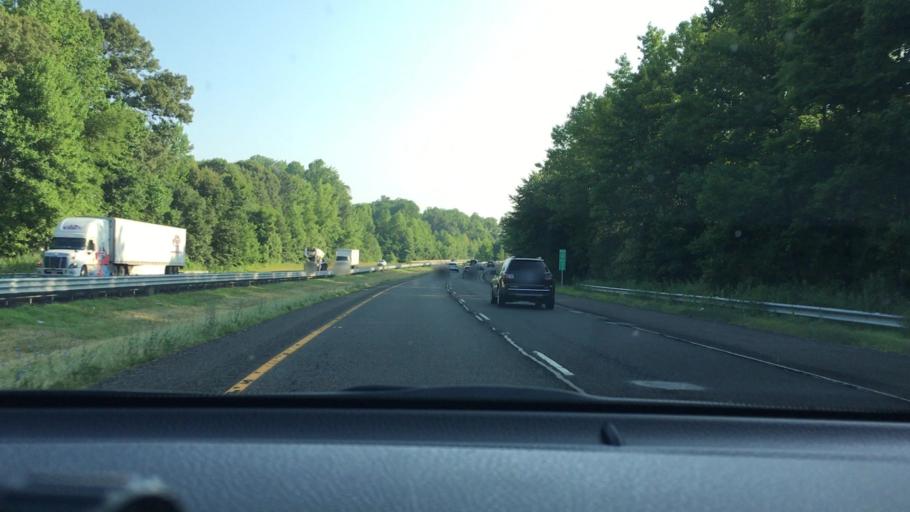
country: US
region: New Jersey
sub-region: Gloucester County
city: Pitman
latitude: 39.7381
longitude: -75.1492
